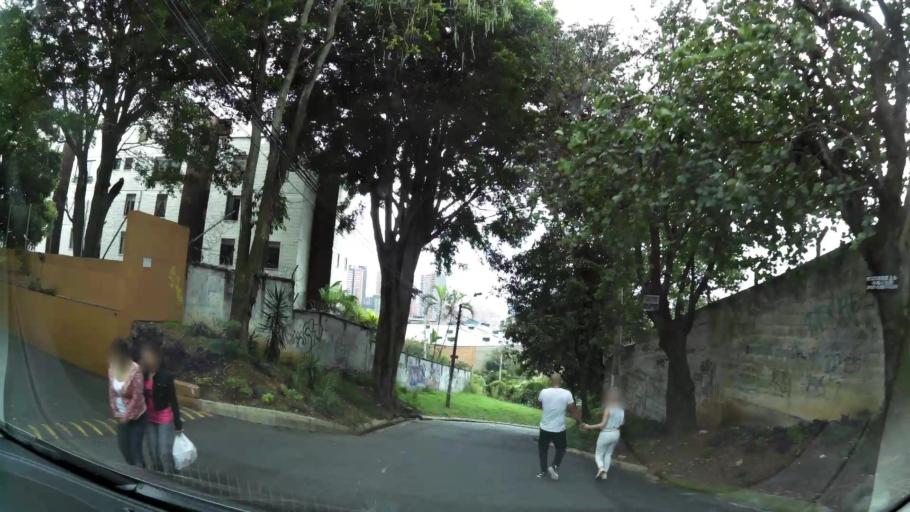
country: CO
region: Antioquia
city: Medellin
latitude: 6.2739
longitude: -75.5943
